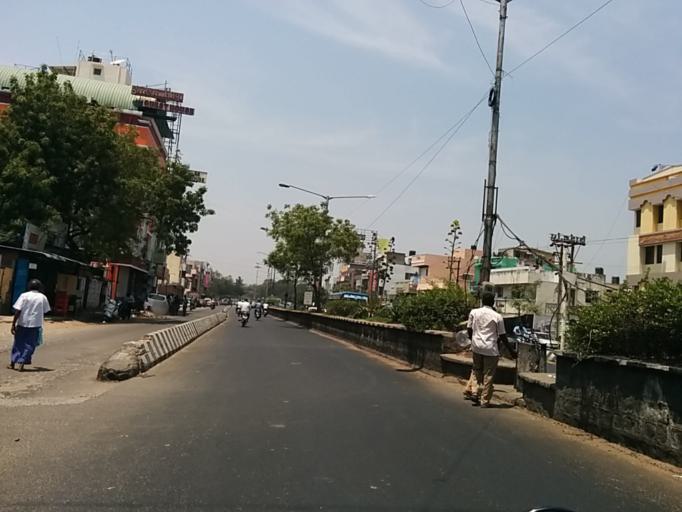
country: IN
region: Pondicherry
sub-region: Puducherry
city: Puducherry
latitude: 11.9321
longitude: 79.8148
